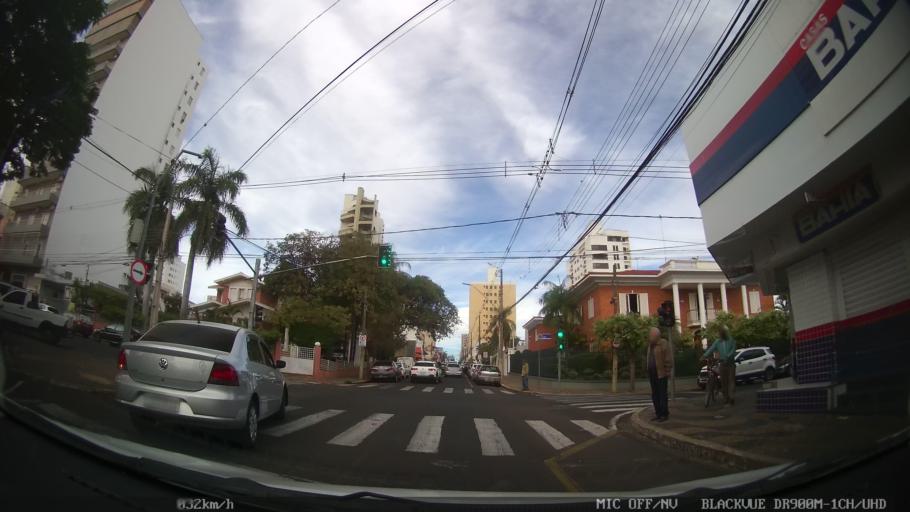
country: BR
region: Sao Paulo
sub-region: Catanduva
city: Catanduva
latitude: -21.1357
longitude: -48.9733
